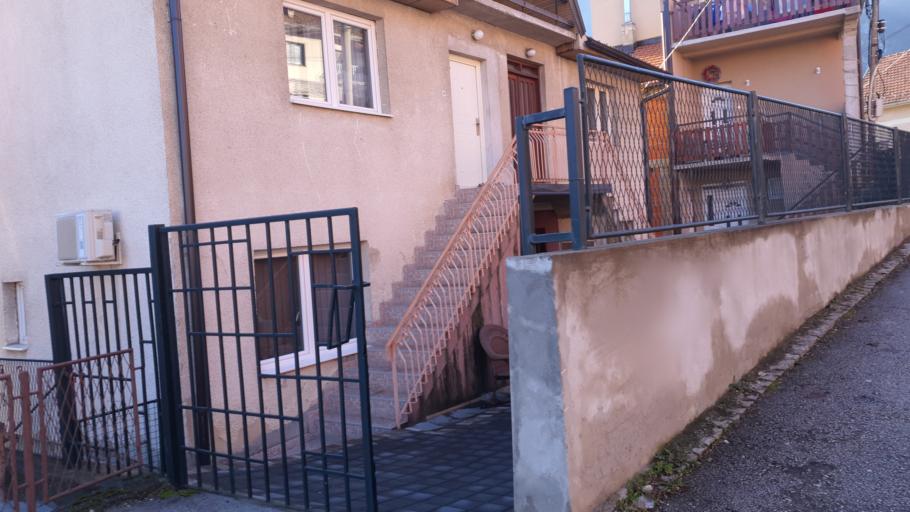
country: RS
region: Central Serbia
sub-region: Zlatiborski Okrug
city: Uzice
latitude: 43.8543
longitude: 19.8318
